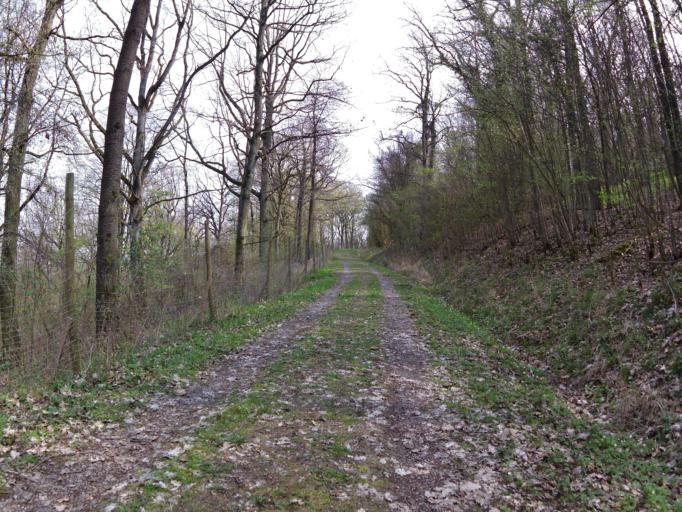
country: DE
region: Bavaria
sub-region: Regierungsbezirk Unterfranken
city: Gerbrunn
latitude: 49.7841
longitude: 10.0118
